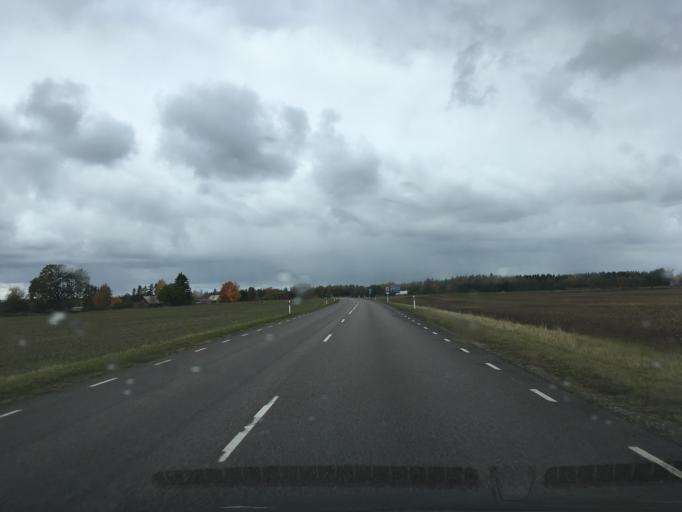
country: EE
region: Harju
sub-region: Anija vald
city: Kehra
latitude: 59.3277
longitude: 25.3248
